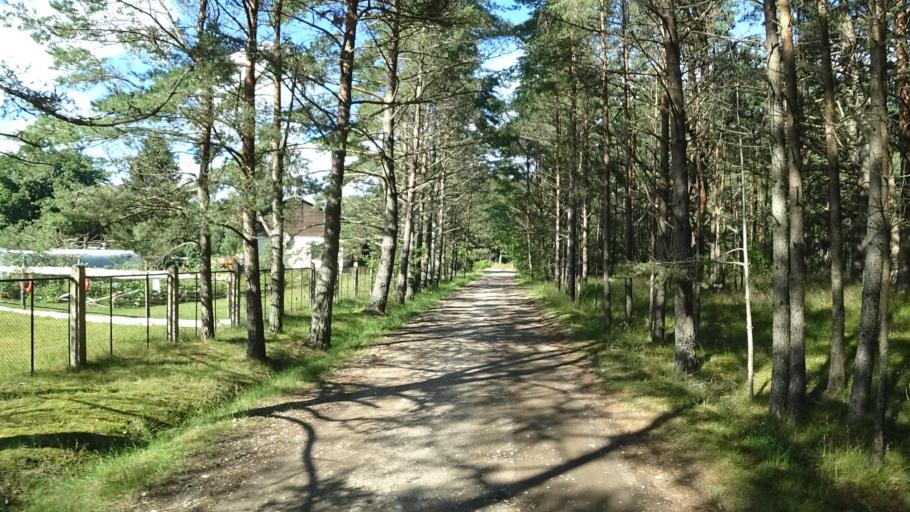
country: LV
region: Ventspils
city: Ventspils
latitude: 57.4884
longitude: 21.6480
